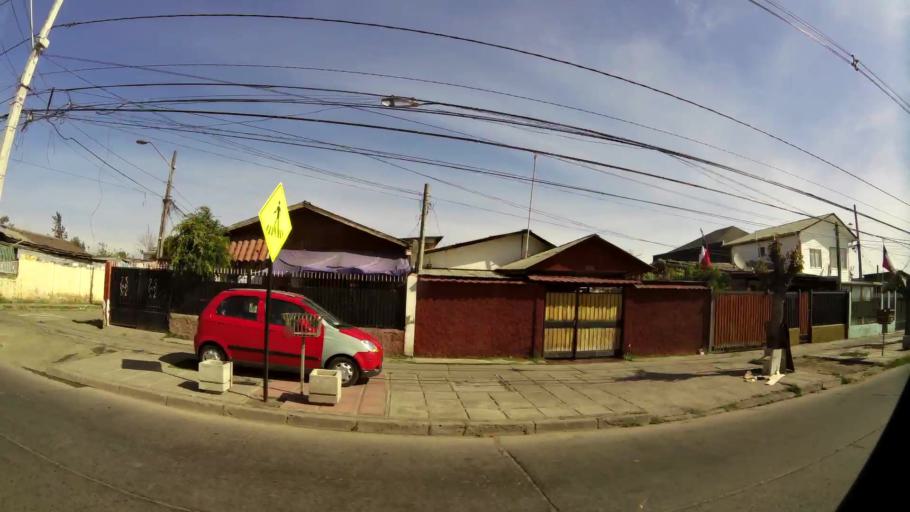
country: CL
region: Santiago Metropolitan
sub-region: Provincia de Santiago
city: La Pintana
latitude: -33.5378
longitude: -70.6380
